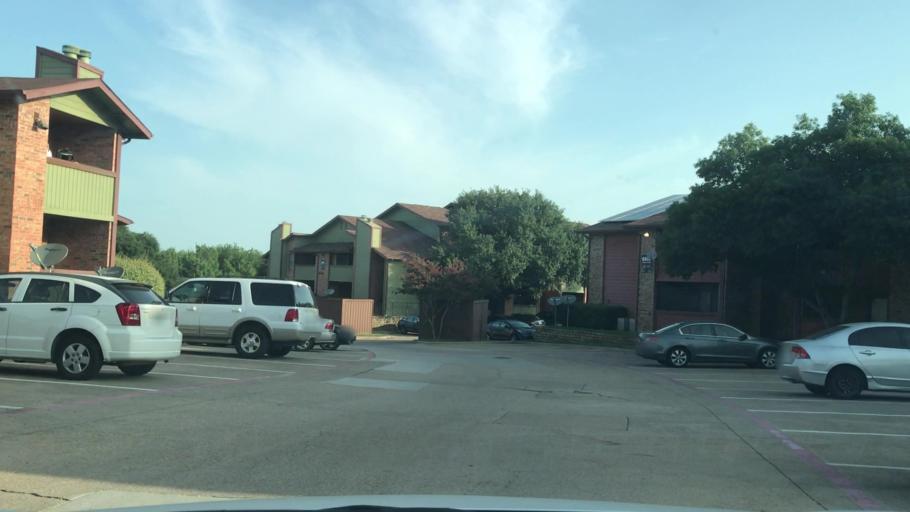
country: US
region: Texas
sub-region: Tarrant County
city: Pantego
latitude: 32.7608
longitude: -97.1620
